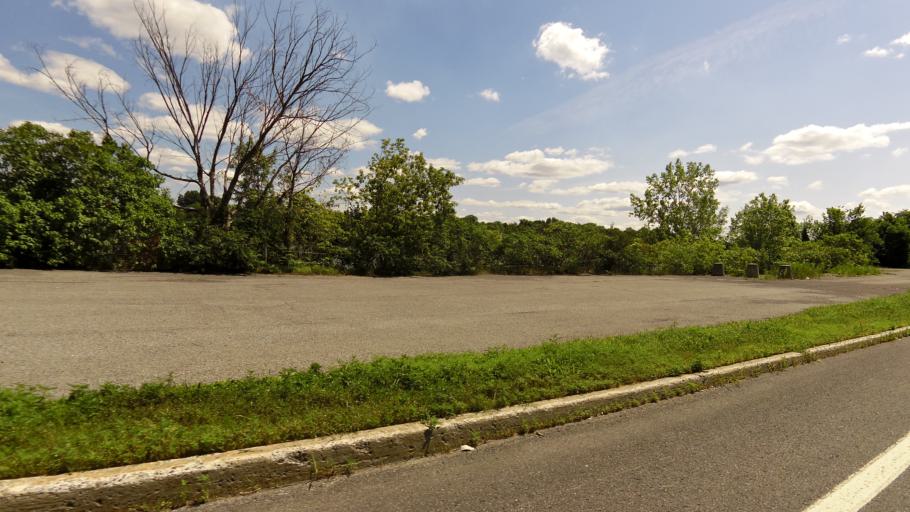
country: CA
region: Quebec
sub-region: Monteregie
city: Richelieu
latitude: 45.4402
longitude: -73.2581
